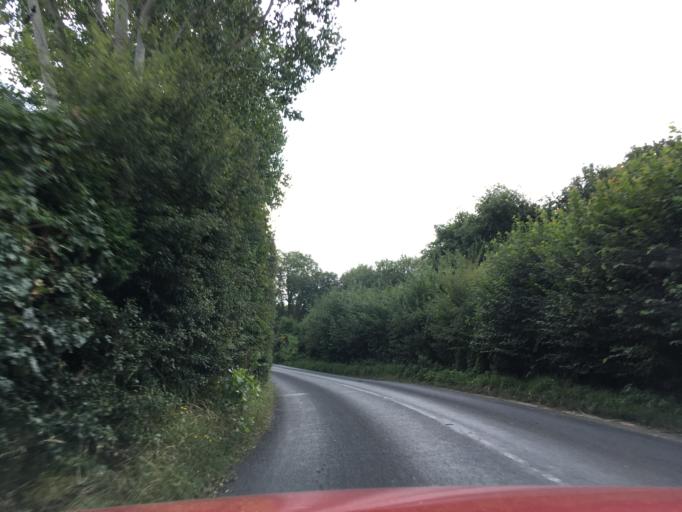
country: GB
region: England
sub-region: Kent
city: Cranbrook
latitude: 51.1132
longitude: 0.5560
